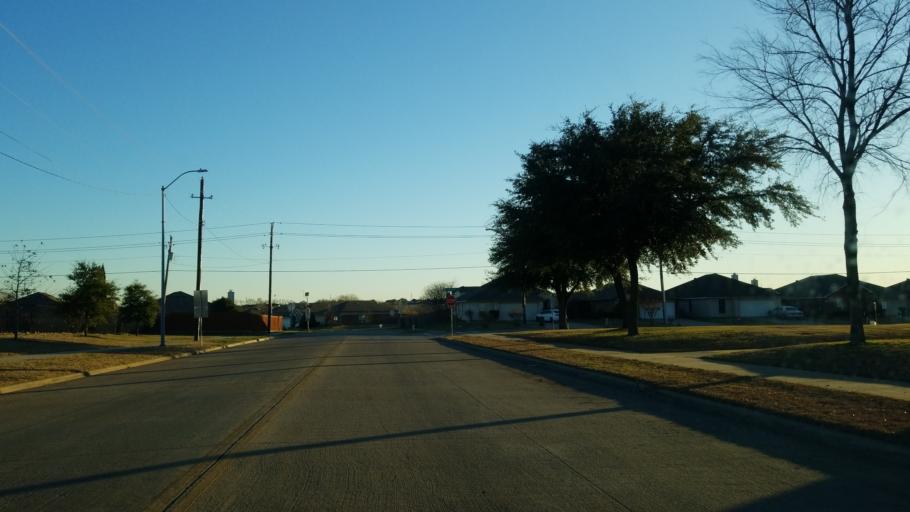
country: US
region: Texas
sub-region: Tarrant County
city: Arlington
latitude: 32.7286
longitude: -97.0540
